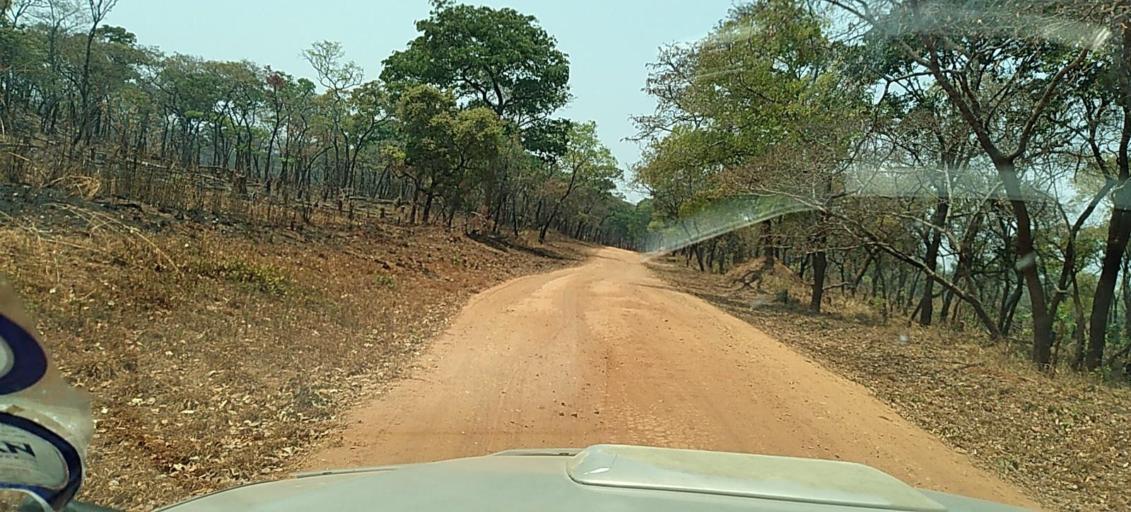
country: ZM
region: North-Western
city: Kasempa
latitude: -13.5446
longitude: 26.0456
